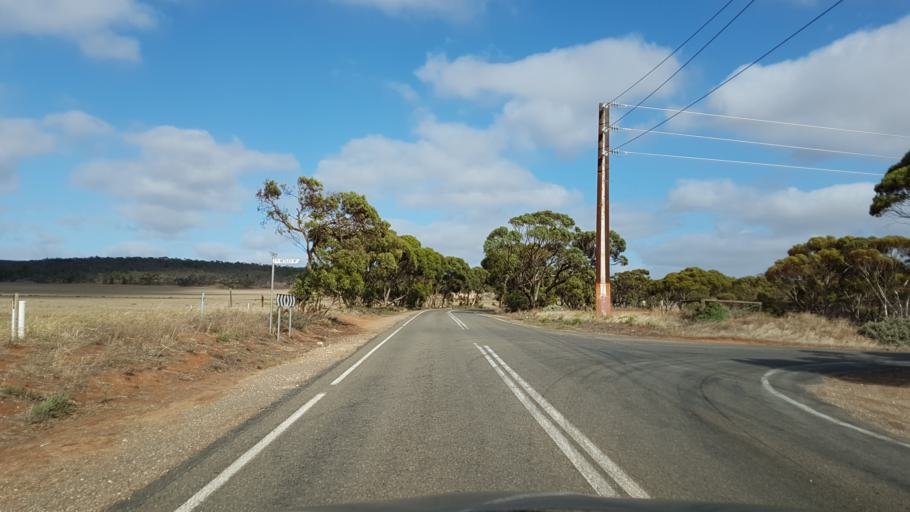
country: AU
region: South Australia
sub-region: Murray Bridge
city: Murray Bridge
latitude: -35.1177
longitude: 139.2373
